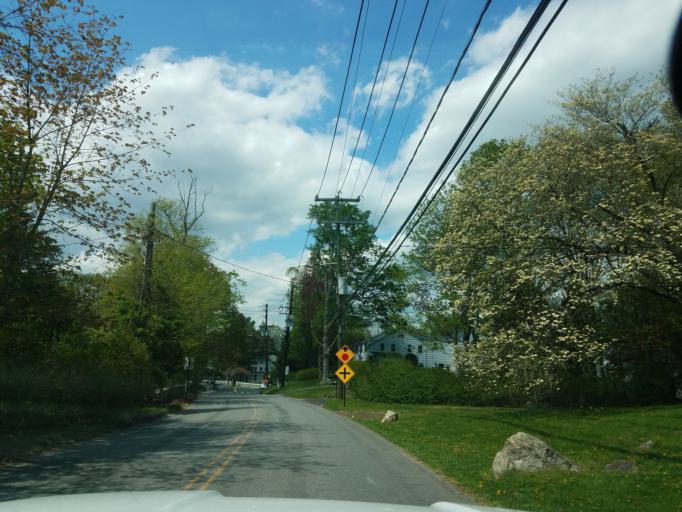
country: US
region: Connecticut
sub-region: Fairfield County
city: New Canaan
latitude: 41.1353
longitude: -73.4799
